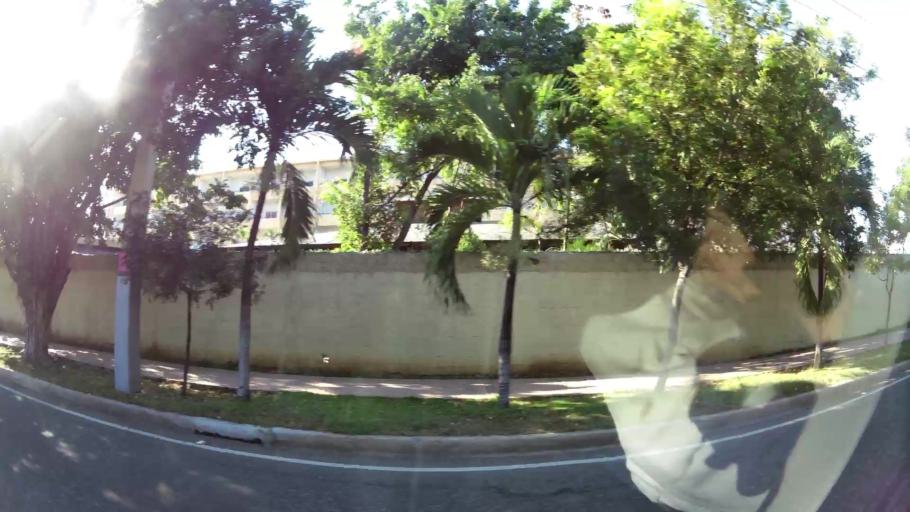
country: DO
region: Nacional
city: La Julia
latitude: 18.4546
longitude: -69.9223
